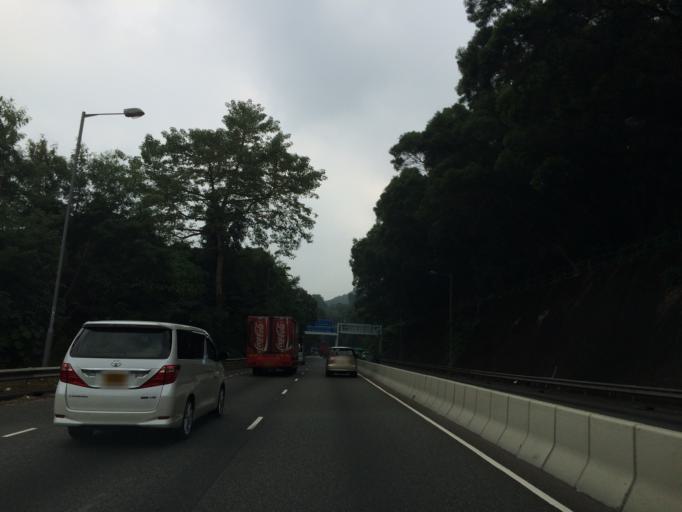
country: HK
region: Wong Tai Sin
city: Wong Tai Sin
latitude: 22.3661
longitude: 114.1848
